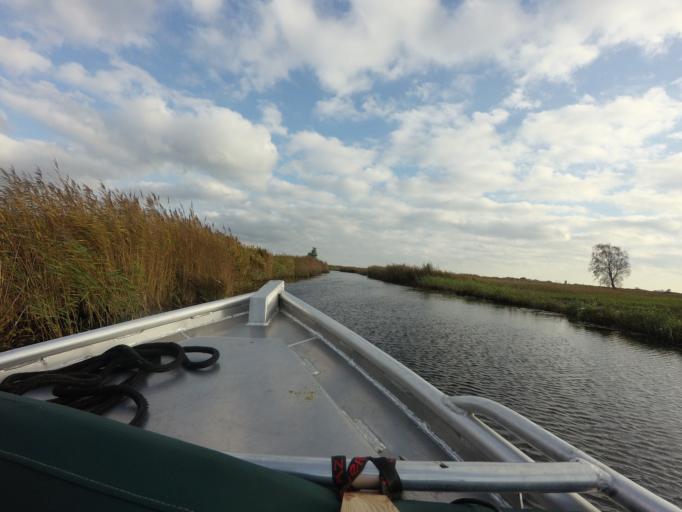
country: NL
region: Overijssel
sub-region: Gemeente Steenwijkerland
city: Blokzijl
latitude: 52.7583
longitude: 5.9512
